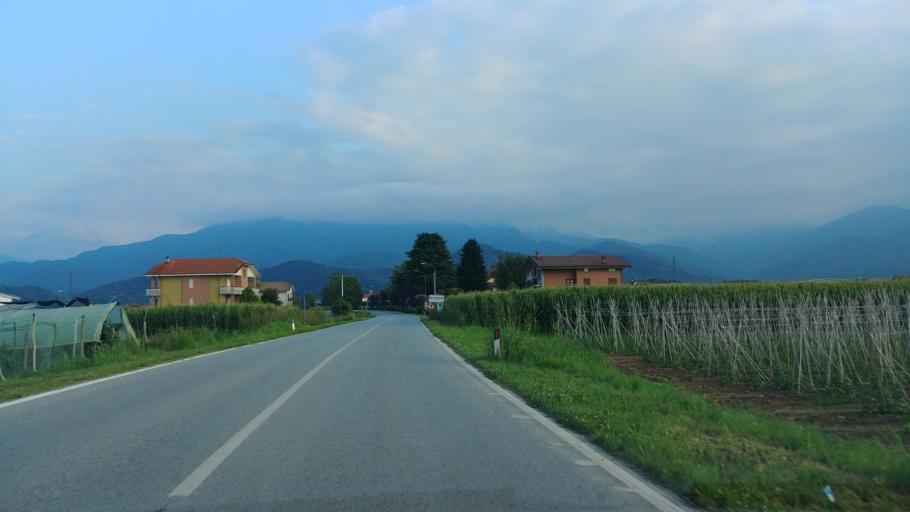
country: IT
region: Piedmont
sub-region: Provincia di Cuneo
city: Peveragno
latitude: 44.3558
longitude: 7.5911
